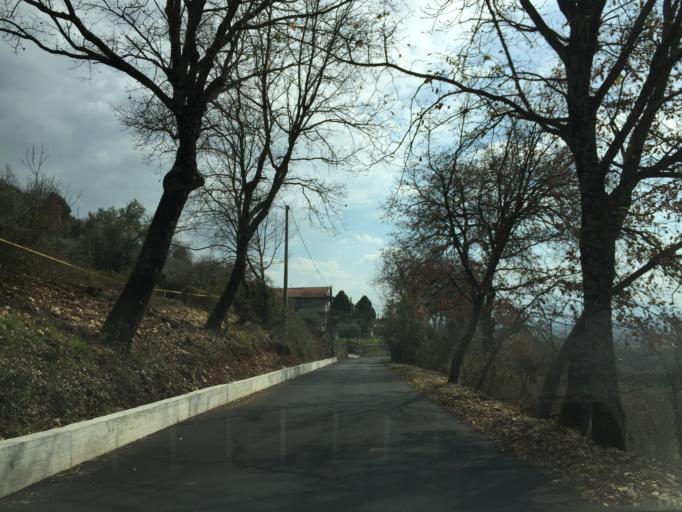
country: IT
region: Latium
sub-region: Provincia di Frosinone
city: Castrocielo
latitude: 41.5229
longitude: 13.7045
